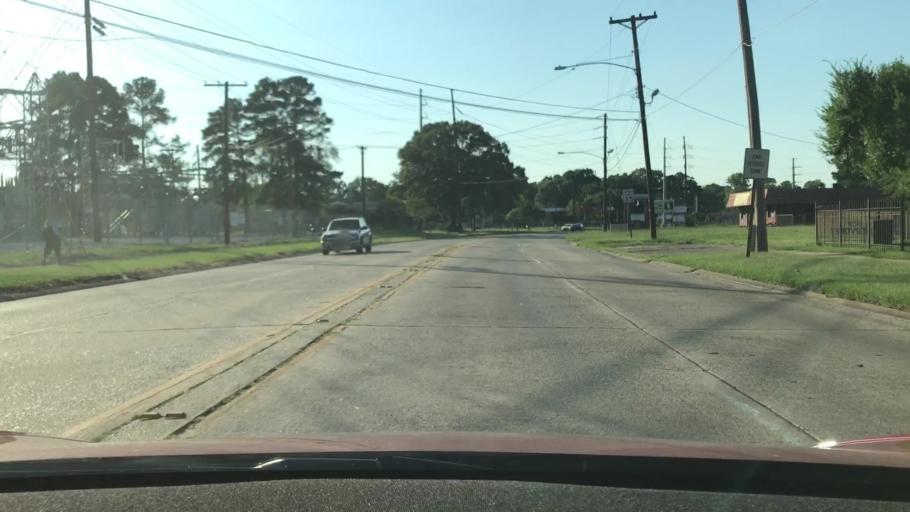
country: US
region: Louisiana
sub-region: Bossier Parish
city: Bossier City
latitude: 32.4305
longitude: -93.7447
